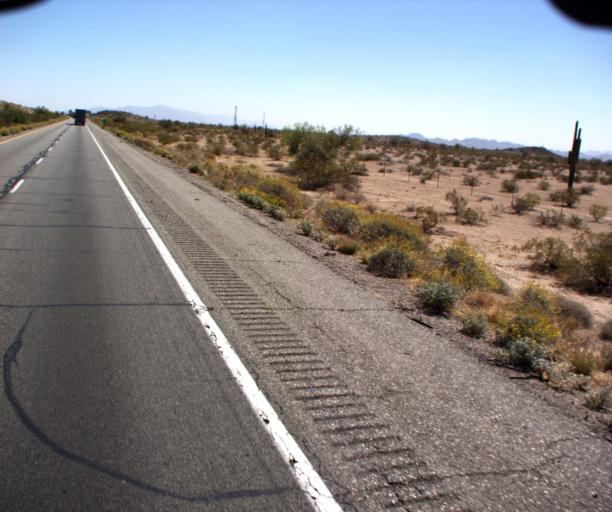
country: US
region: Arizona
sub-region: Maricopa County
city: Buckeye
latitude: 33.4335
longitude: -112.6537
